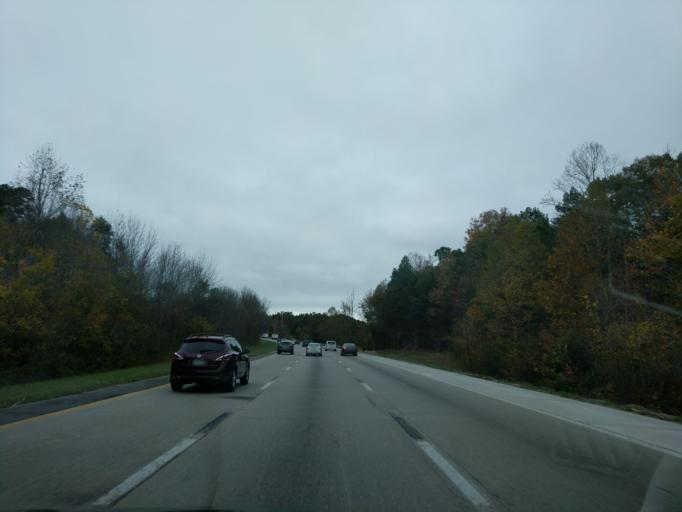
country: US
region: North Carolina
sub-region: Guilford County
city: Jamestown
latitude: 35.9381
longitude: -79.9080
